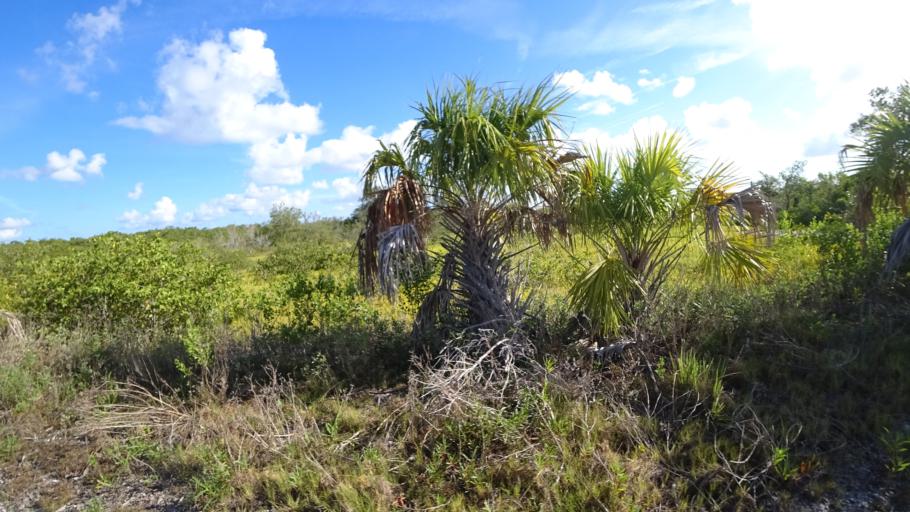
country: US
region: Florida
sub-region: Manatee County
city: Holmes Beach
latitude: 27.5145
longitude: -82.6727
